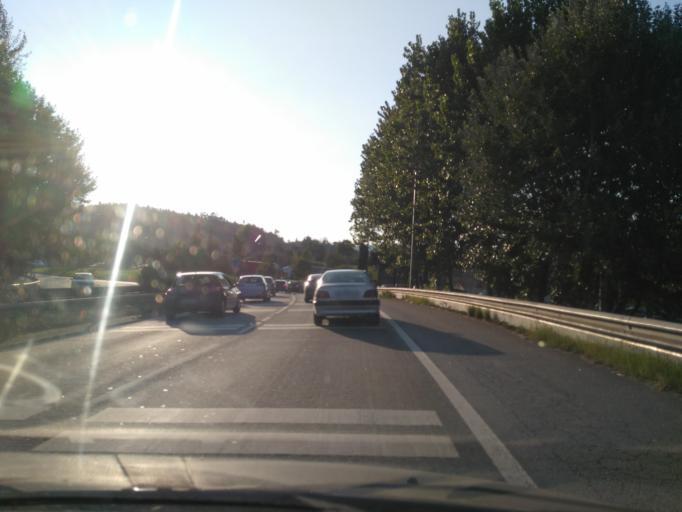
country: PT
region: Braga
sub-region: Guimaraes
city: Candoso
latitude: 41.4401
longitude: -8.3313
